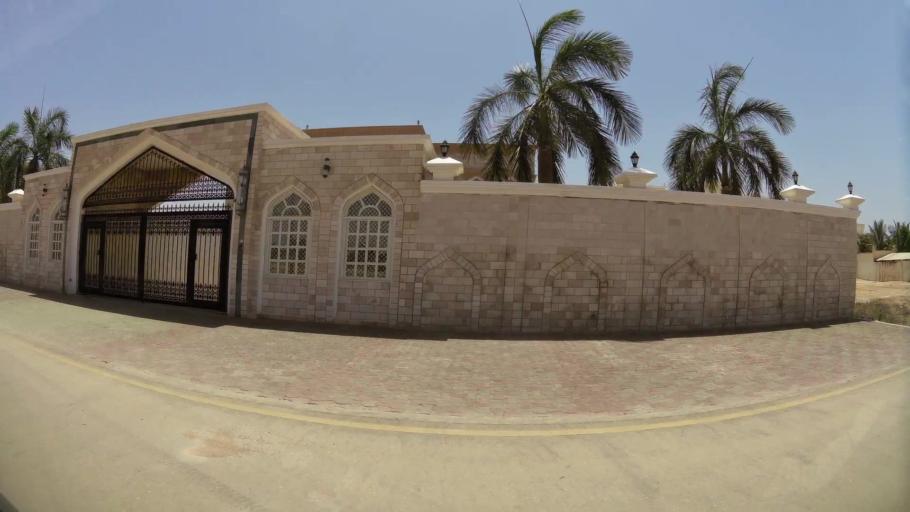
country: OM
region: Zufar
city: Salalah
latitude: 17.0652
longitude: 54.1490
